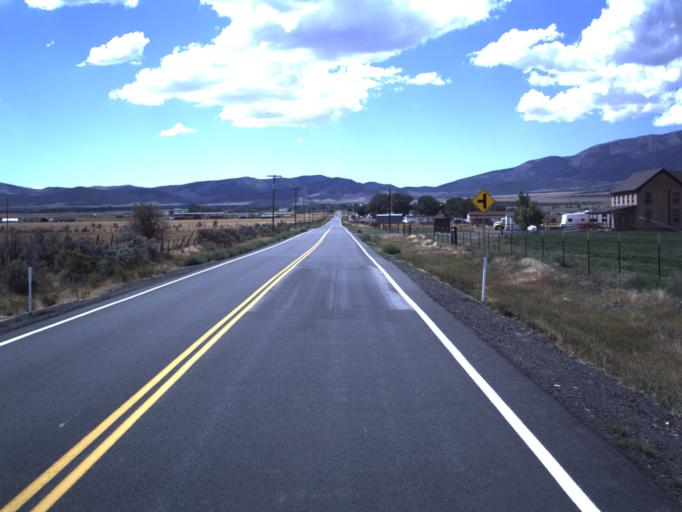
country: US
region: Utah
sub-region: Tooele County
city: Tooele
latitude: 40.3368
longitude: -112.4344
